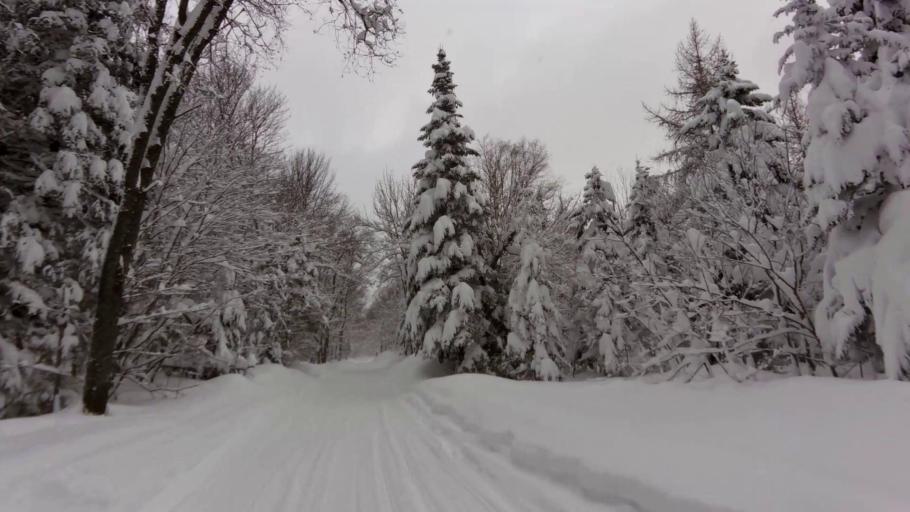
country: US
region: New York
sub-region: Lewis County
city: Lowville
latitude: 43.7316
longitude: -75.6377
